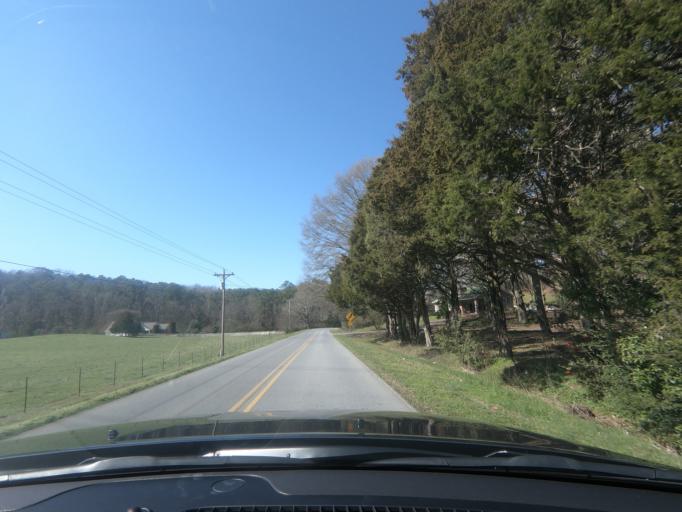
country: US
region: Georgia
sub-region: Gordon County
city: Calhoun
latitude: 34.4614
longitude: -84.9952
